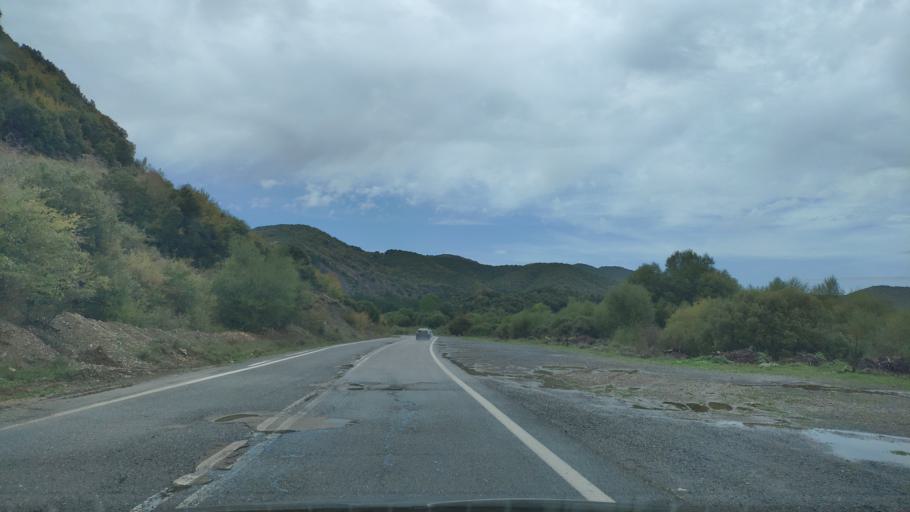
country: GR
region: Peloponnese
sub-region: Nomos Arkadias
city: Dimitsana
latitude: 37.6281
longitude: 22.0687
